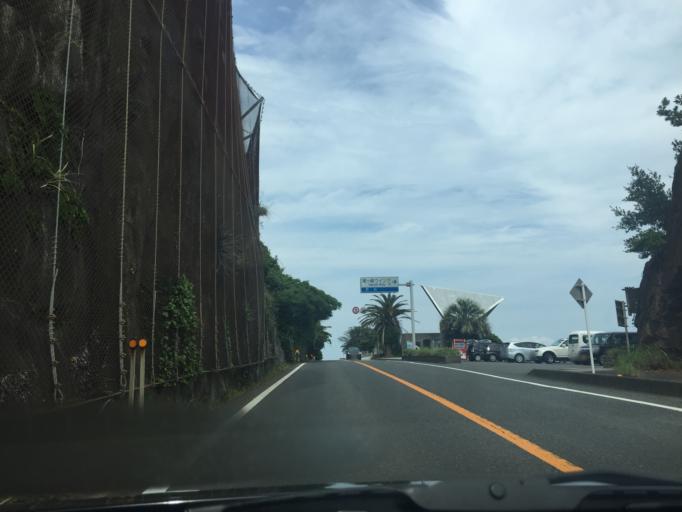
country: JP
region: Shizuoka
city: Shimoda
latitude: 34.7153
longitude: 138.9871
